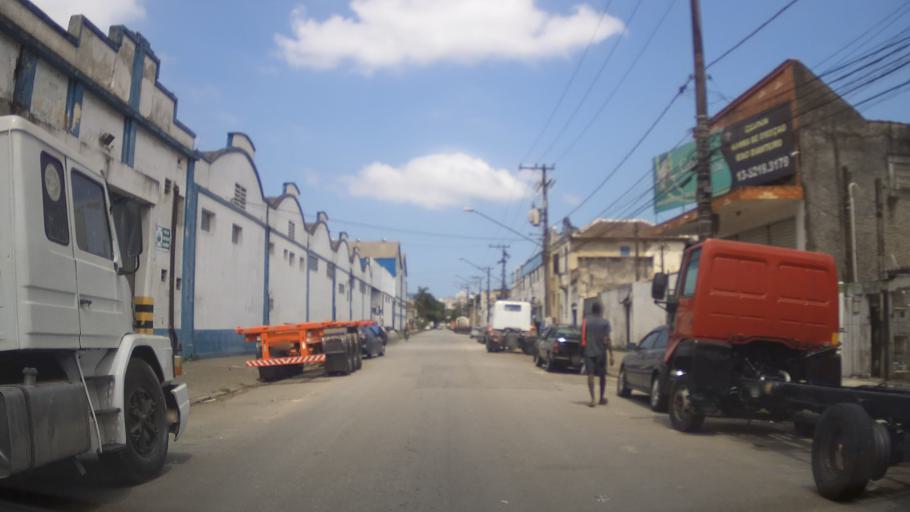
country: BR
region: Sao Paulo
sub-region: Santos
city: Santos
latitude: -23.9531
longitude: -46.3142
